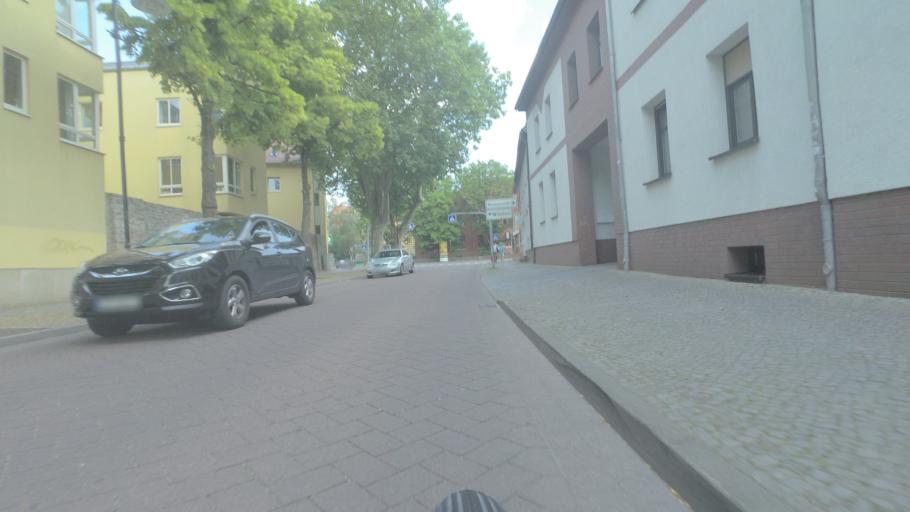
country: DE
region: Saxony-Anhalt
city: Koethen
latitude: 51.7498
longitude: 11.9719
